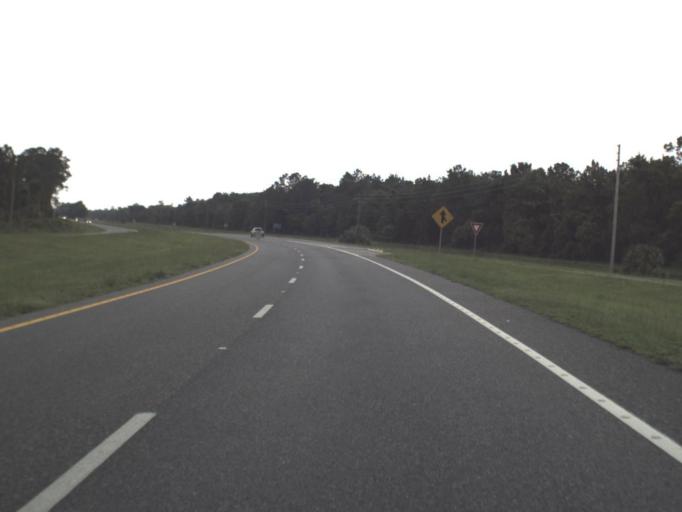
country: US
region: Florida
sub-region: Levy County
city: Inglis
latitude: 29.1655
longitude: -82.6413
